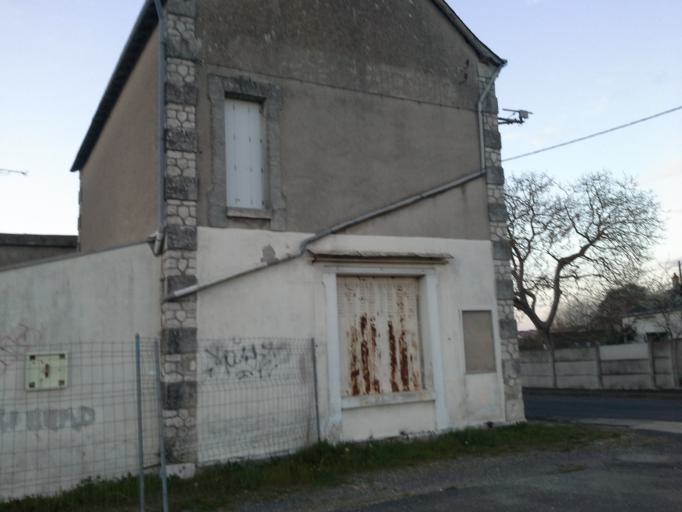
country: FR
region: Centre
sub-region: Departement du Loir-et-Cher
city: Vendome
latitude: 47.8029
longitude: 1.0672
